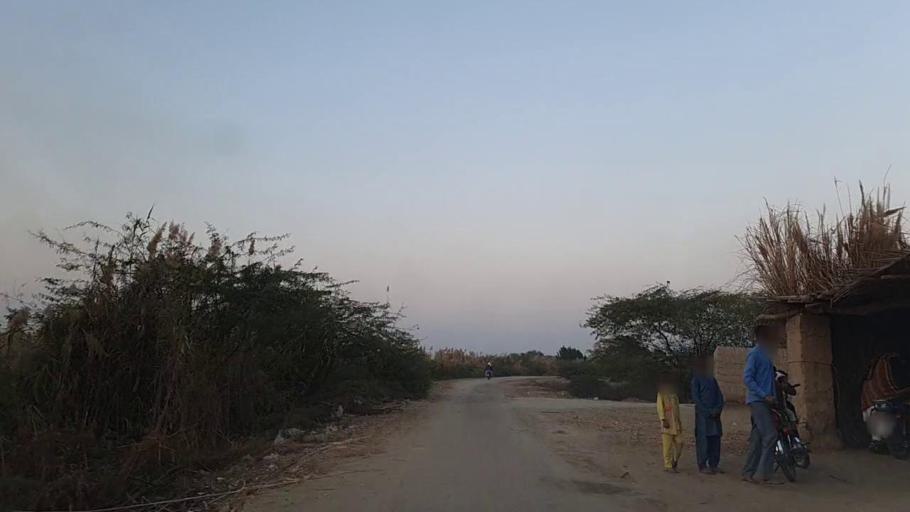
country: PK
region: Sindh
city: Bandhi
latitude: 26.6022
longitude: 68.3653
